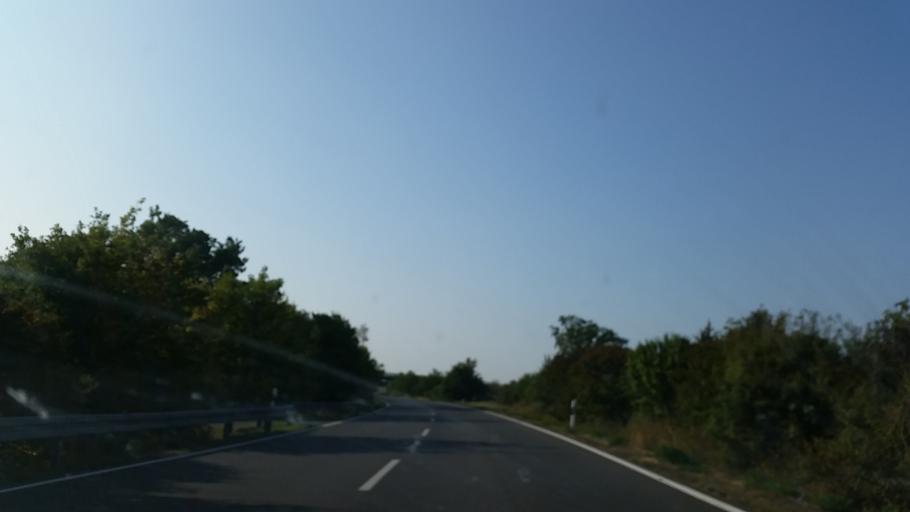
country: DE
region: Brandenburg
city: Zichow
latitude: 53.1953
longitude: 14.0446
